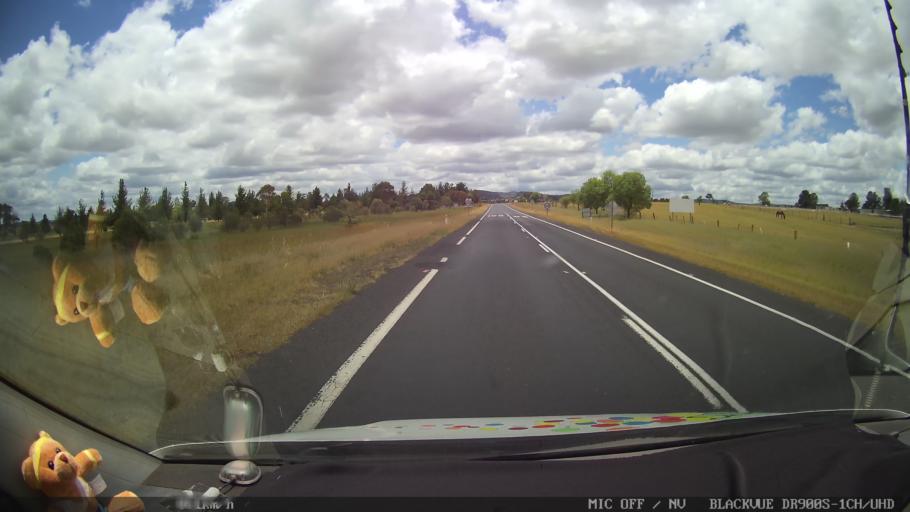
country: AU
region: New South Wales
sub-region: Glen Innes Severn
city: Glen Innes
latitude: -29.4351
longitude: 151.8484
